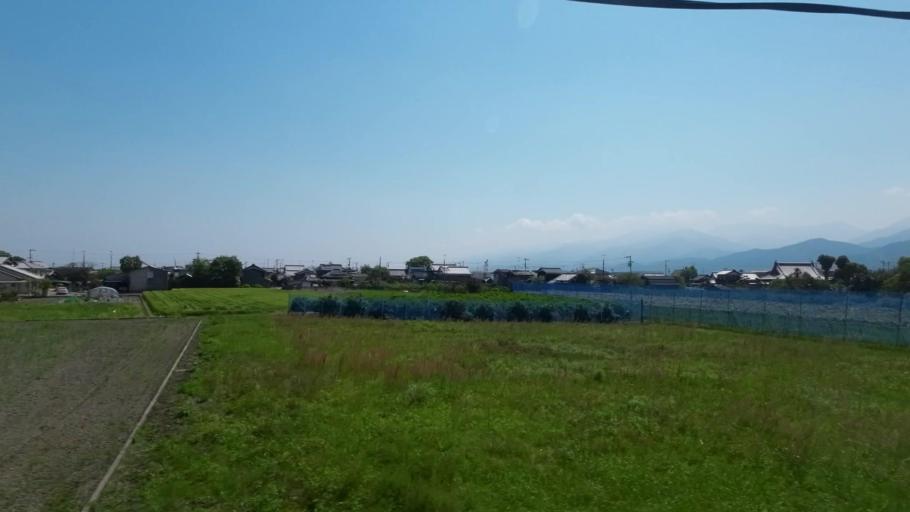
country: JP
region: Ehime
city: Saijo
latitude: 33.9103
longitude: 133.0991
